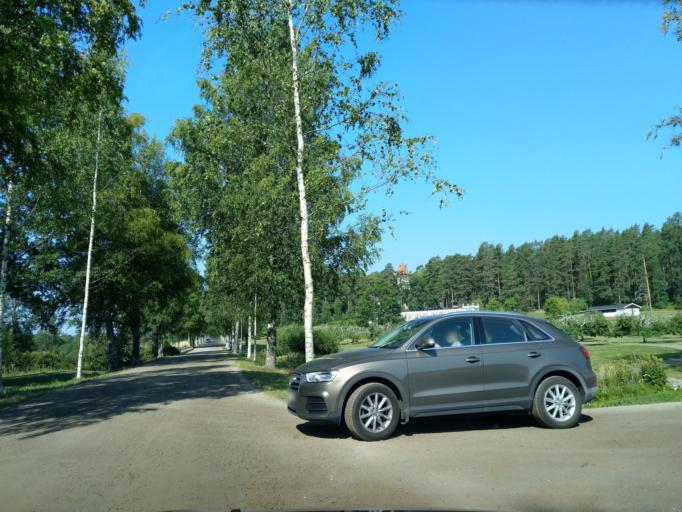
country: FI
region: Satakunta
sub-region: Pori
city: Noormarkku
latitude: 61.5950
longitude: 21.8782
